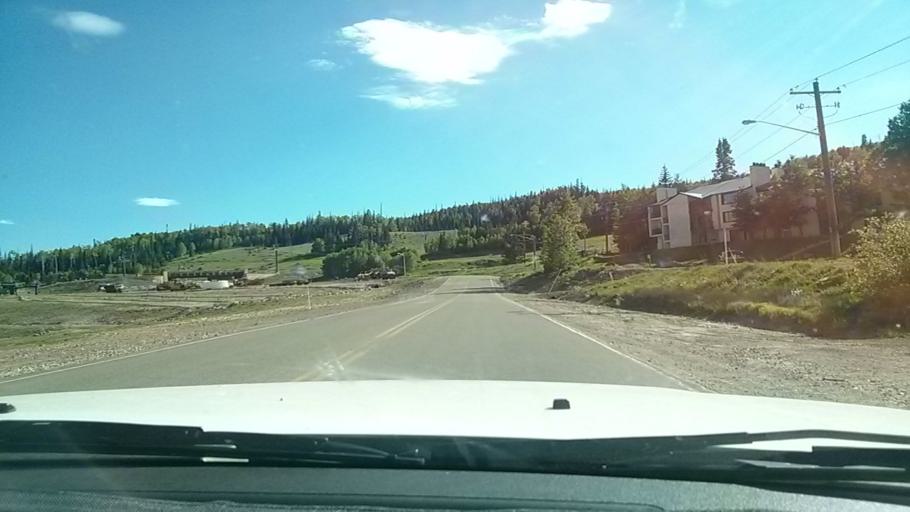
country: US
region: Utah
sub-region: Iron County
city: Parowan
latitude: 37.6913
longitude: -112.8517
